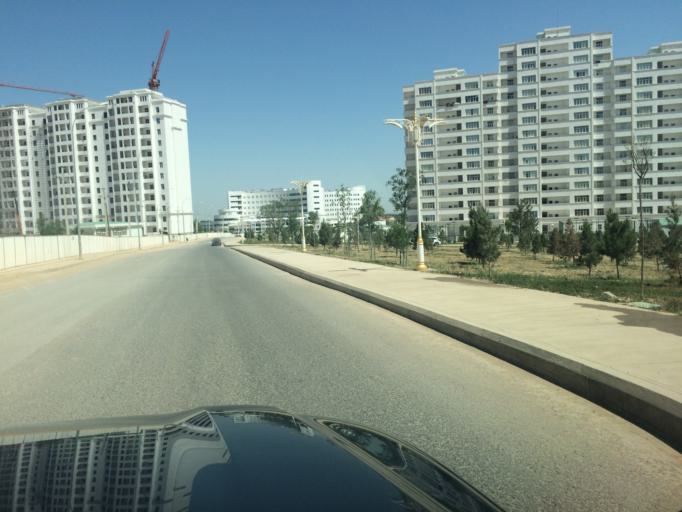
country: TM
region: Ahal
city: Ashgabat
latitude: 37.9368
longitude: 58.3628
